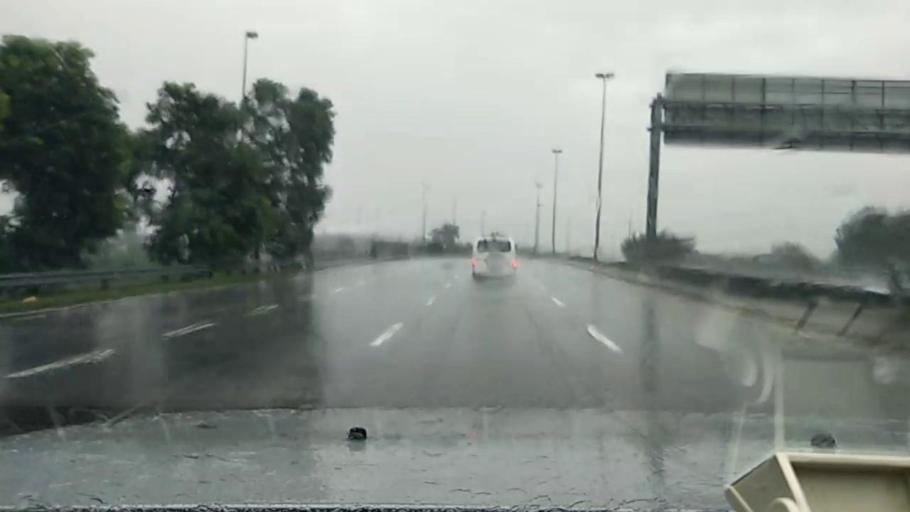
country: MY
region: Selangor
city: Kampong Baharu Balakong
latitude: 2.9950
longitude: 101.7743
